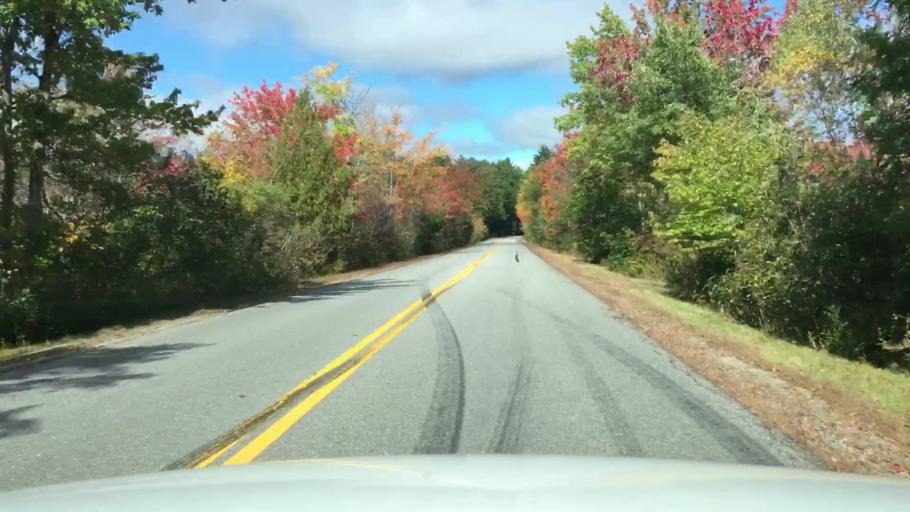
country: US
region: Maine
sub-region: Sagadahoc County
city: North Bath
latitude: 43.9545
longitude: -69.8946
